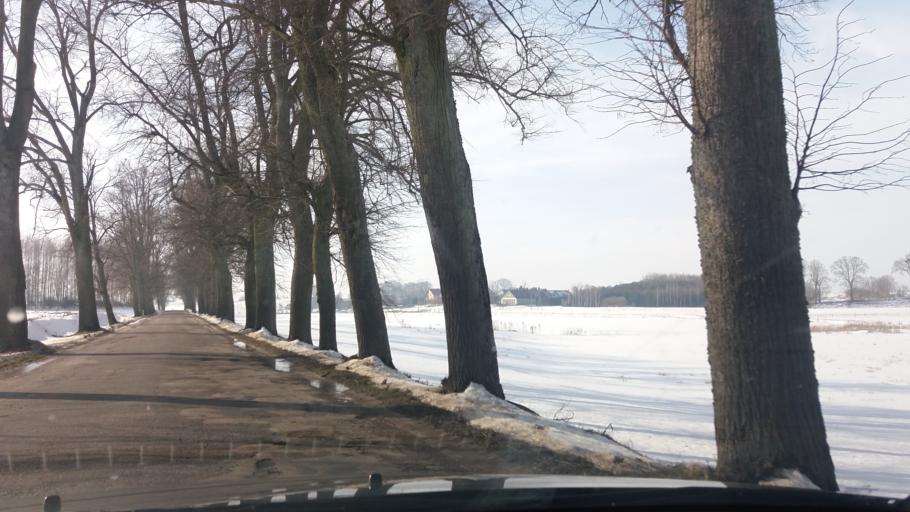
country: PL
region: Warmian-Masurian Voivodeship
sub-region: Powiat bartoszycki
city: Bisztynek
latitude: 54.1032
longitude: 20.8115
